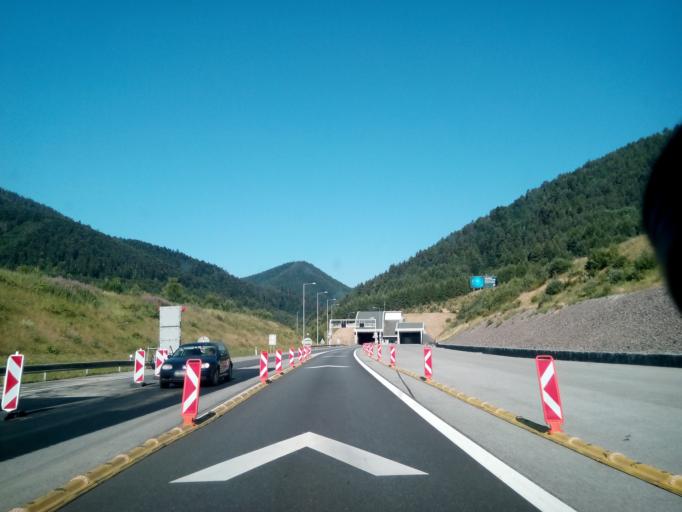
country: SK
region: Kosicky
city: Krompachy
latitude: 48.9961
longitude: 20.9096
